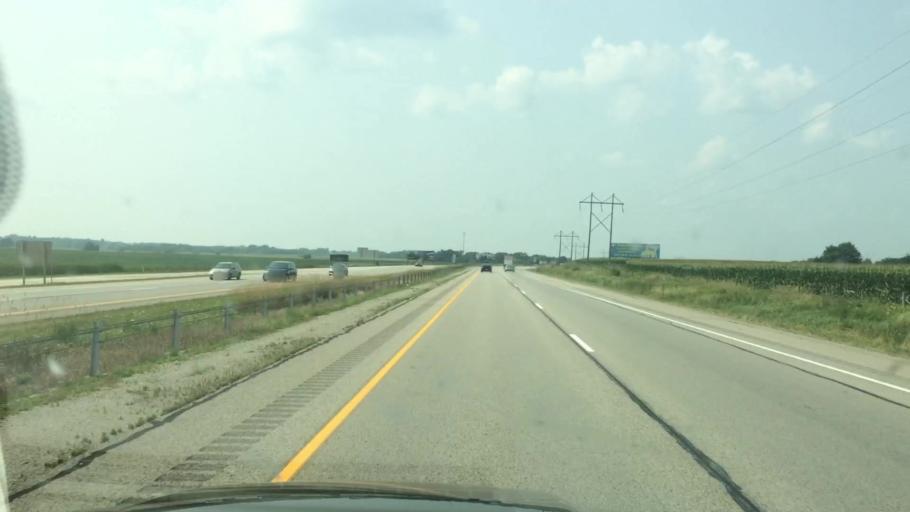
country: US
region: Wisconsin
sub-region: Fond du Lac County
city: North Fond du Lac
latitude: 43.8525
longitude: -88.5743
